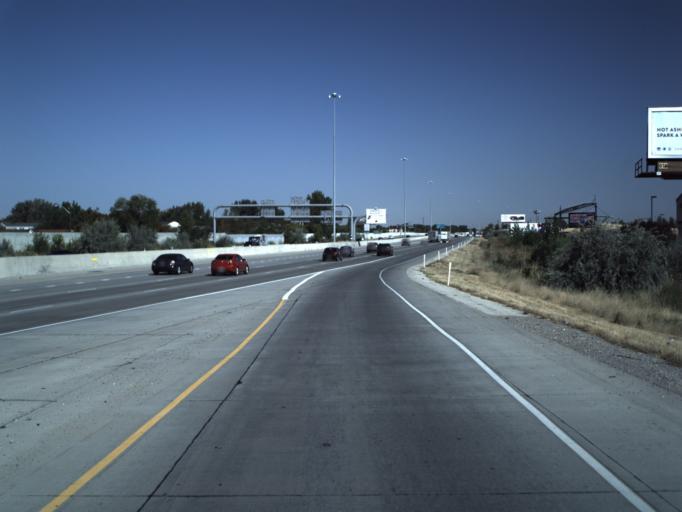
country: US
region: Utah
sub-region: Salt Lake County
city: Salt Lake City
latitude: 40.7844
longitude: -111.9113
